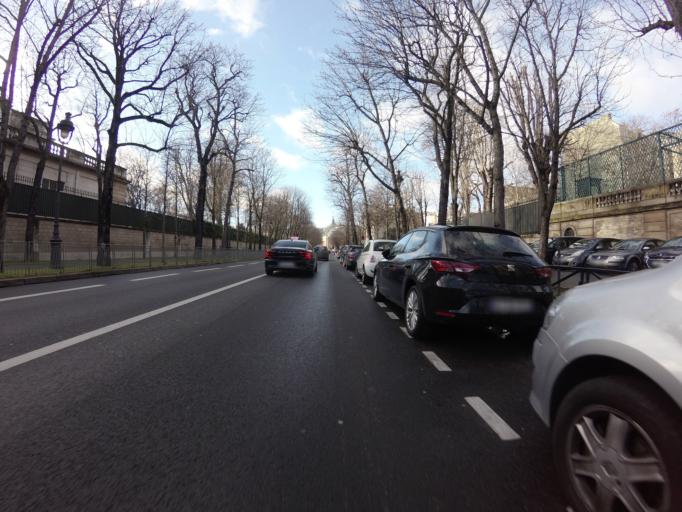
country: FR
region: Ile-de-France
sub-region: Departement des Hauts-de-Seine
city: Clichy
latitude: 48.8701
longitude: 2.3156
